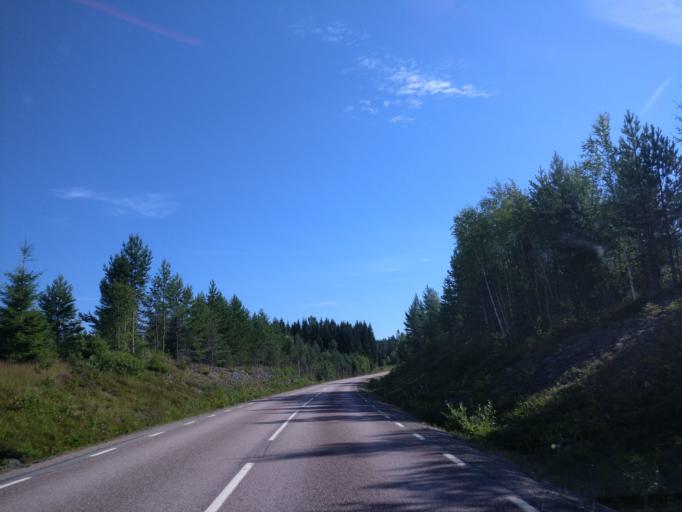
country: SE
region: Vaermland
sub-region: Hagfors Kommun
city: Hagfors
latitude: 60.0412
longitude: 13.9262
